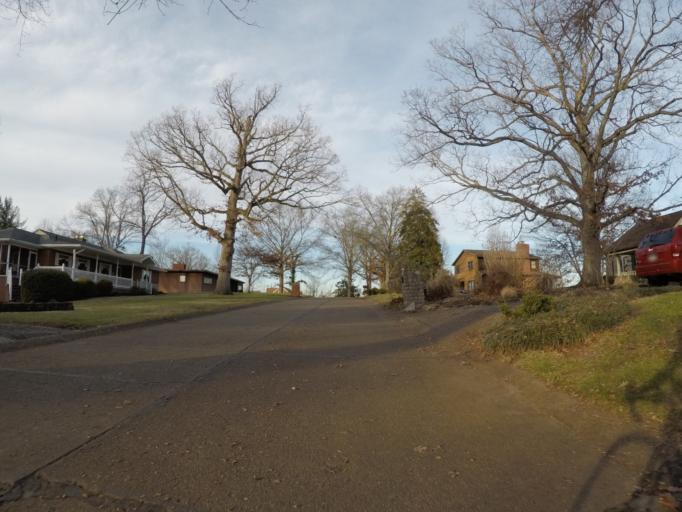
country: US
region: West Virginia
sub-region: Cabell County
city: Huntington
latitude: 38.4056
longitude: -82.3917
